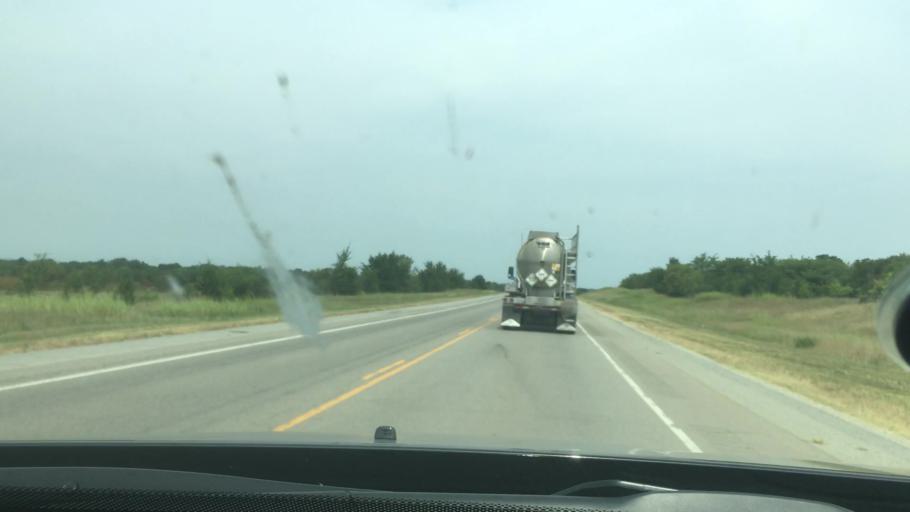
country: US
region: Oklahoma
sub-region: Pontotoc County
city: Ada
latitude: 34.6357
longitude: -96.4775
